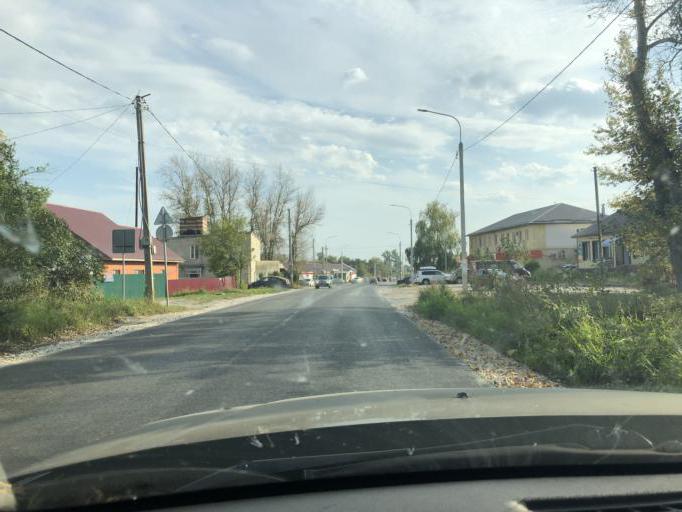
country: RU
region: Tula
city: Leninskiy
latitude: 54.2874
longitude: 37.4661
